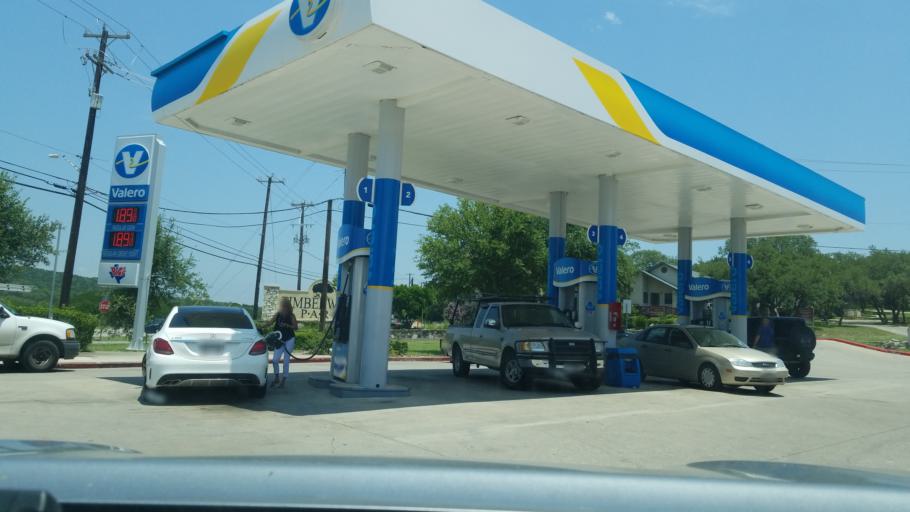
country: US
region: Texas
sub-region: Bexar County
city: Timberwood Park
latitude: 29.6745
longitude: -98.5223
